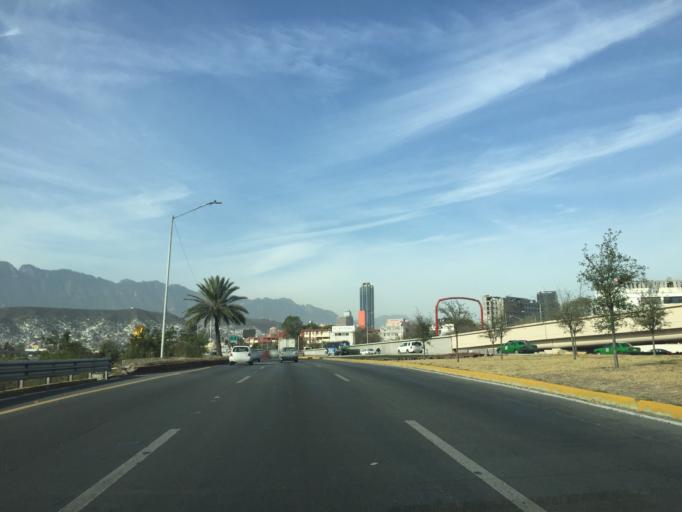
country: MX
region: Nuevo Leon
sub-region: Monterrey
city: Monterrey
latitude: 25.6680
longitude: -100.2991
